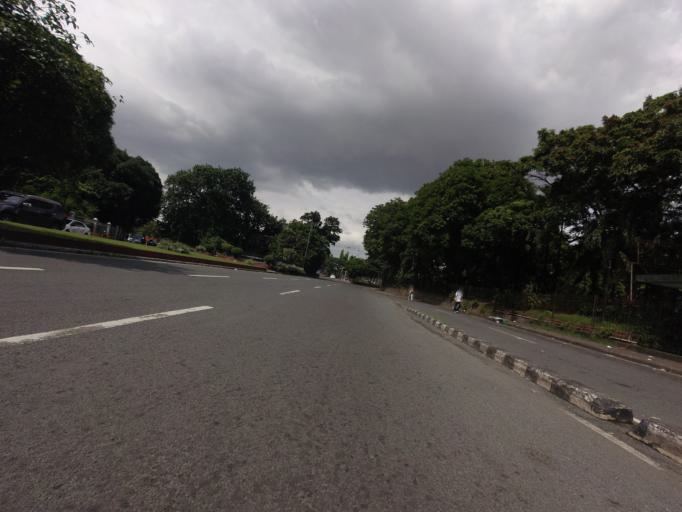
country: PH
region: Metro Manila
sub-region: City of Manila
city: Port Area
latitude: 14.5844
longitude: 120.9799
